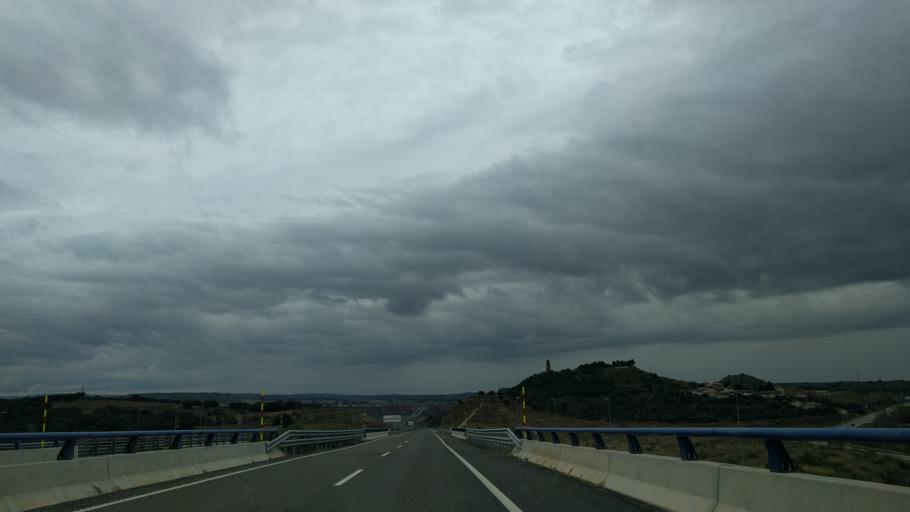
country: ES
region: Aragon
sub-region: Provincia de Huesca
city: Castejon del Puente
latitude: 41.9704
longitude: 0.1511
